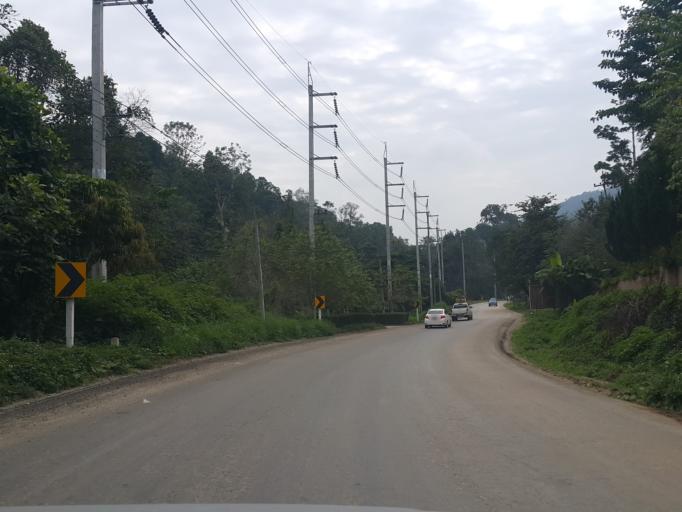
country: TH
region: Chiang Mai
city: Mae Taeng
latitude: 19.1683
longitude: 98.6915
